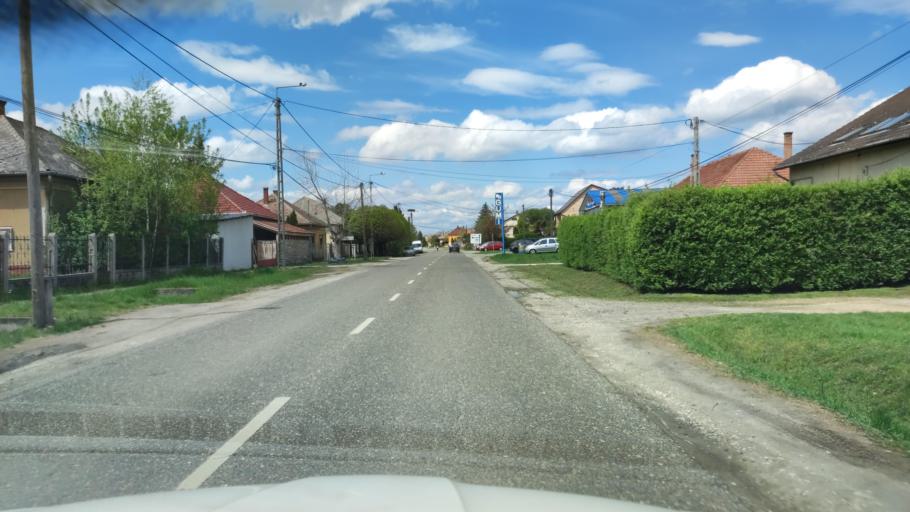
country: HU
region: Pest
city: Tortel
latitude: 47.1223
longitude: 19.9380
